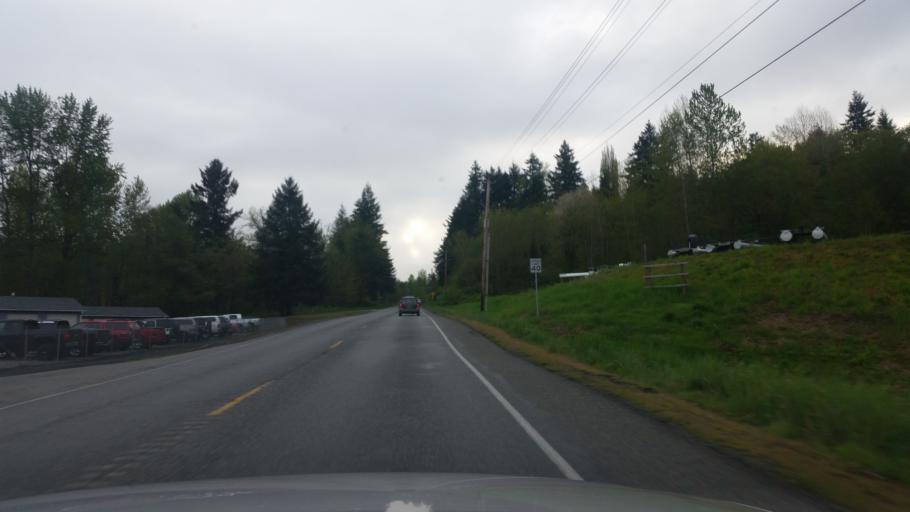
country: US
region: Washington
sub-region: Pierce County
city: Eatonville
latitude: 46.8724
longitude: -122.2664
